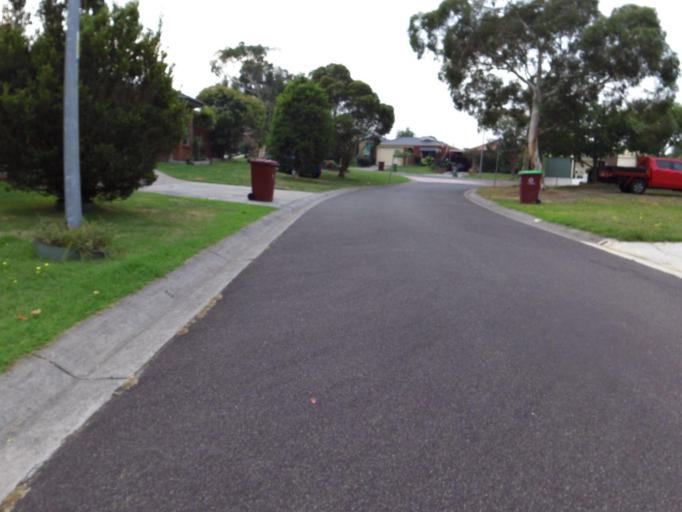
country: AU
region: Victoria
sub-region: Casey
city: Narre Warren
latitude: -38.0167
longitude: 145.3237
